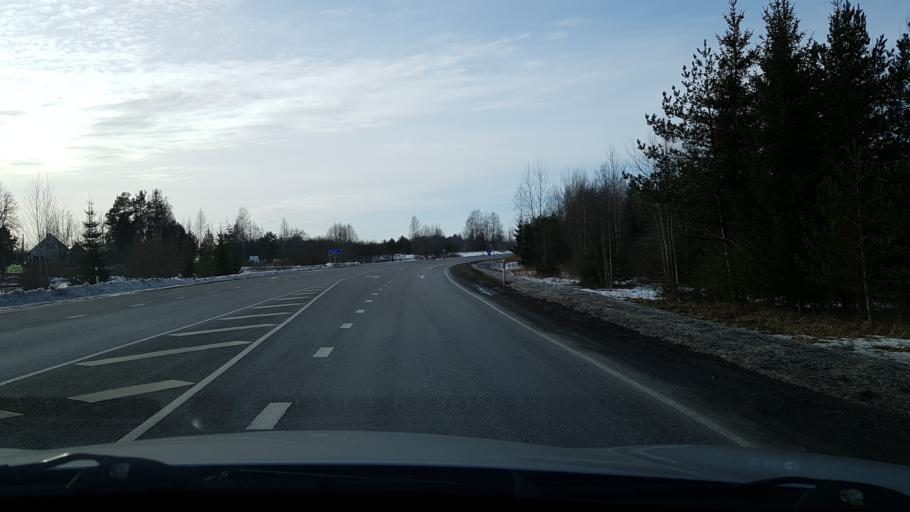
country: EE
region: Viljandimaa
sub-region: Viljandi linn
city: Viljandi
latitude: 58.3389
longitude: 25.4801
